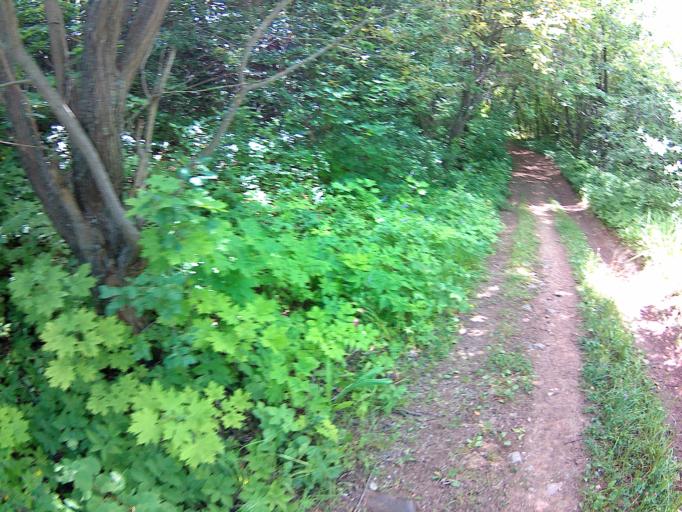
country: RU
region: Nizjnij Novgorod
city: Nizhniy Novgorod
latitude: 56.2375
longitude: 43.9364
